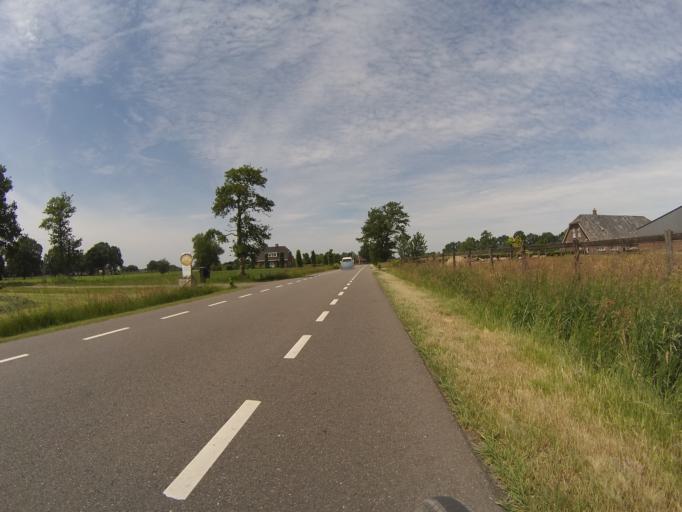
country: NL
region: Gelderland
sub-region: Gemeente Ede
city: Lunteren
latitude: 52.1150
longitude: 5.6254
